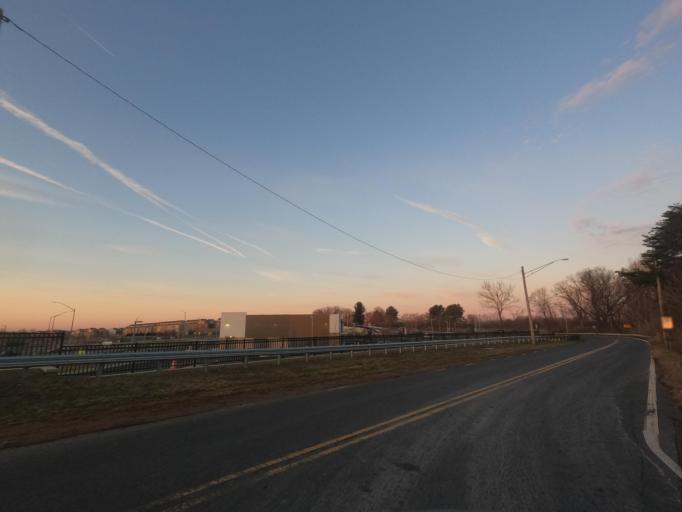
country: US
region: Maryland
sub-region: Montgomery County
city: Clarksburg
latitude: 39.2298
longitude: -77.2884
